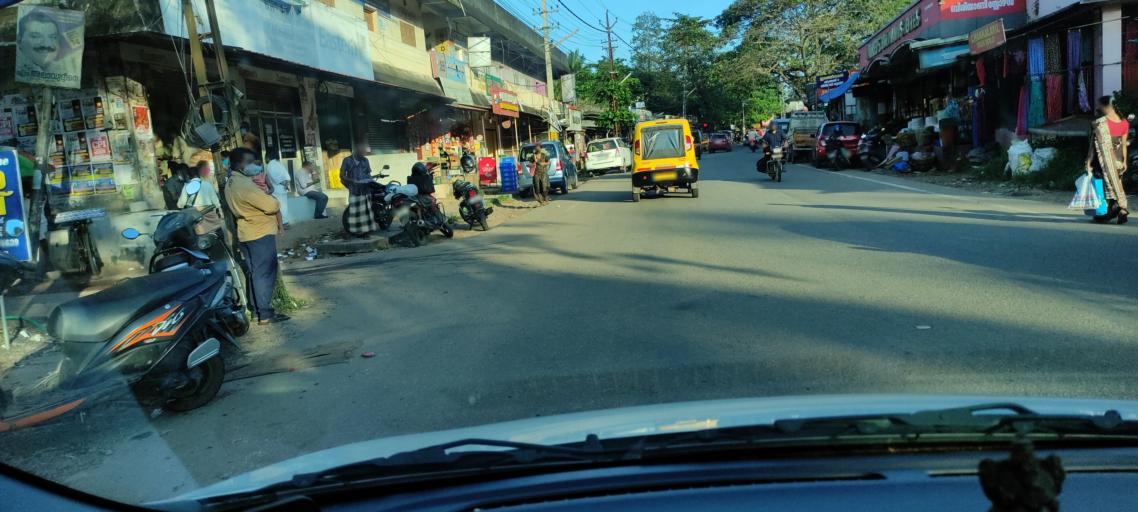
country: IN
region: Kerala
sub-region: Pattanamtitta
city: Adur
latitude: 9.1484
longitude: 76.7599
